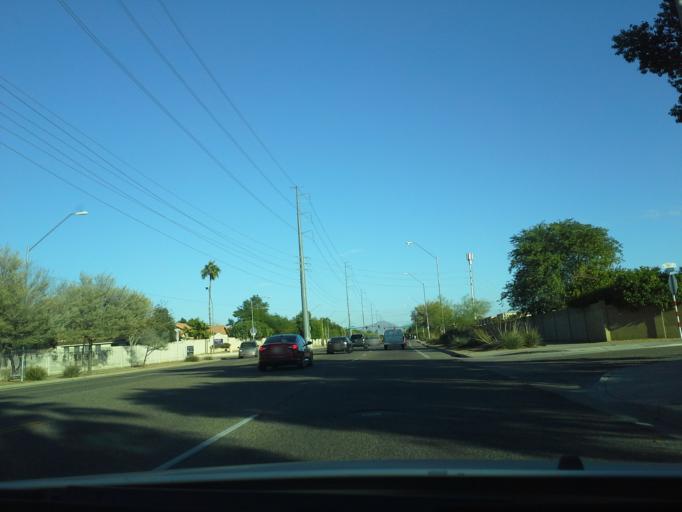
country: US
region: Arizona
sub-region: Maricopa County
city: Paradise Valley
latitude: 33.6549
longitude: -112.0428
